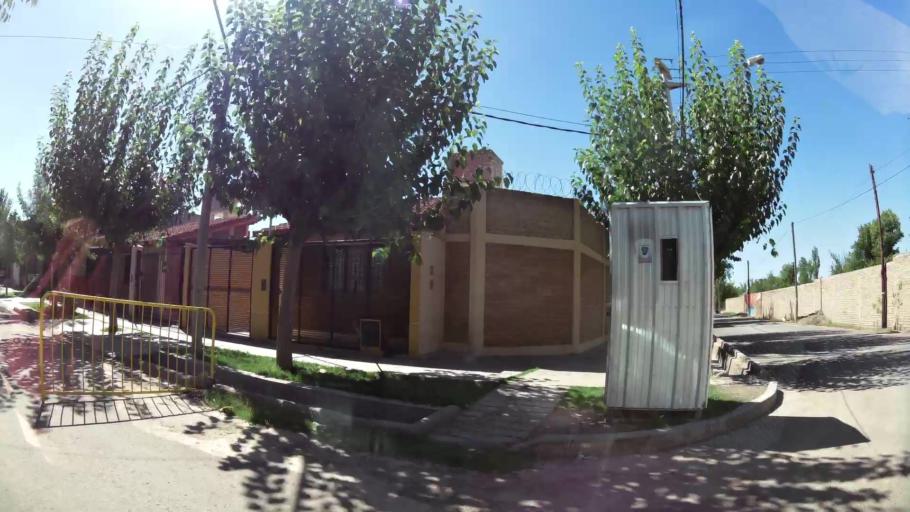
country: AR
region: Mendoza
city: Villa Nueva
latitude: -32.9014
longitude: -68.7741
